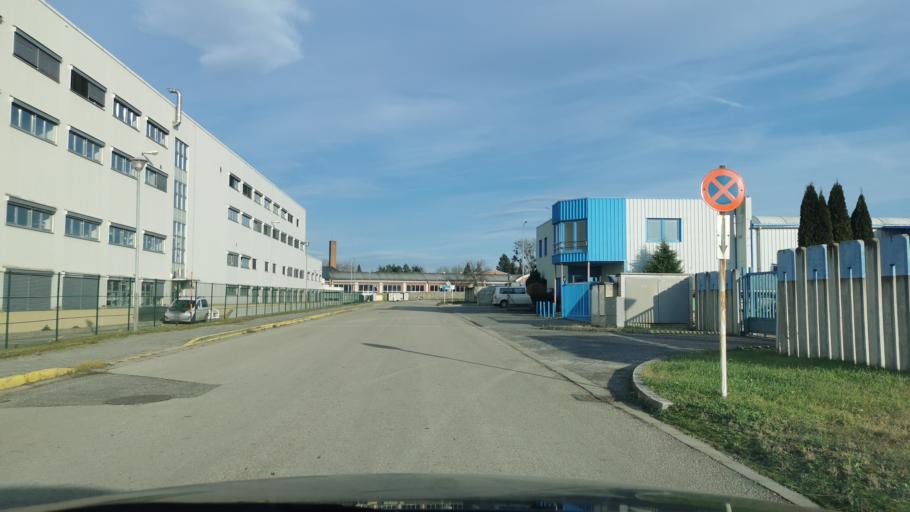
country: SK
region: Trnavsky
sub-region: Okres Skalica
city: Skalica
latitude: 48.8507
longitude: 17.2154
